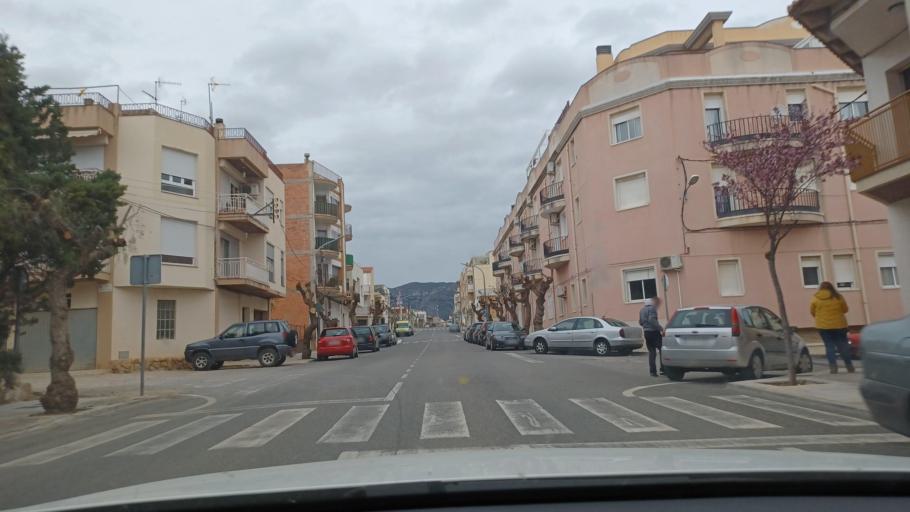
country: ES
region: Valencia
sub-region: Provincia de Castello
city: Rosell
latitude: 40.6316
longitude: 0.2868
